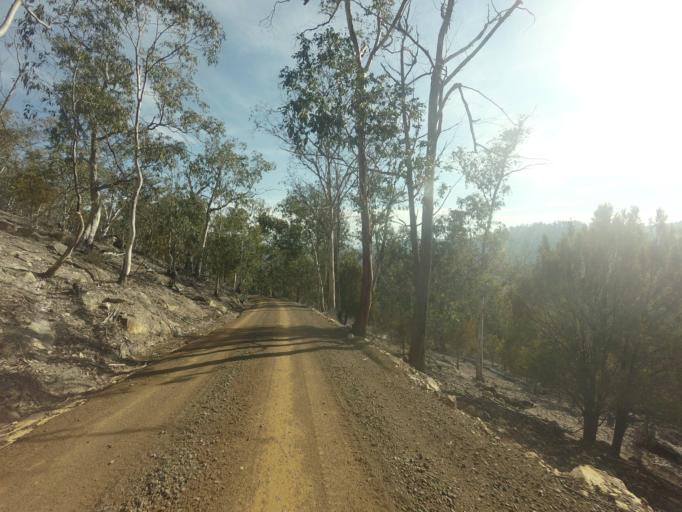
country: AU
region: Tasmania
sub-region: Sorell
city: Sorell
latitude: -42.5271
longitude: 147.4573
